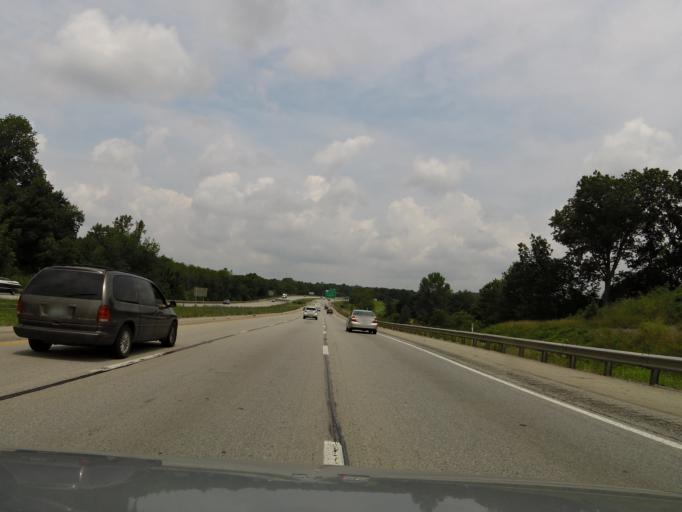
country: US
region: Kentucky
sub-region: Hardin County
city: Elizabethtown
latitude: 37.6841
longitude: -85.8426
